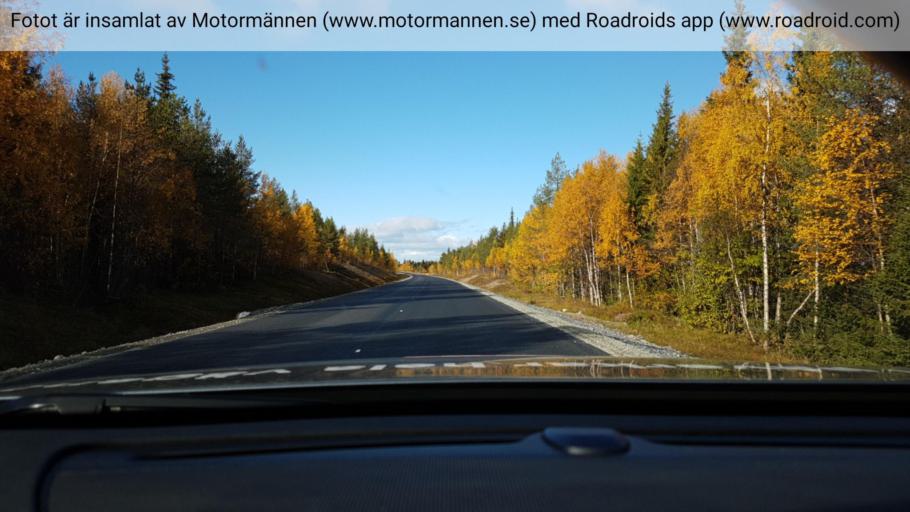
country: SE
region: Norrbotten
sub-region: Arjeplogs Kommun
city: Arjeplog
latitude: 65.9734
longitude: 18.2455
